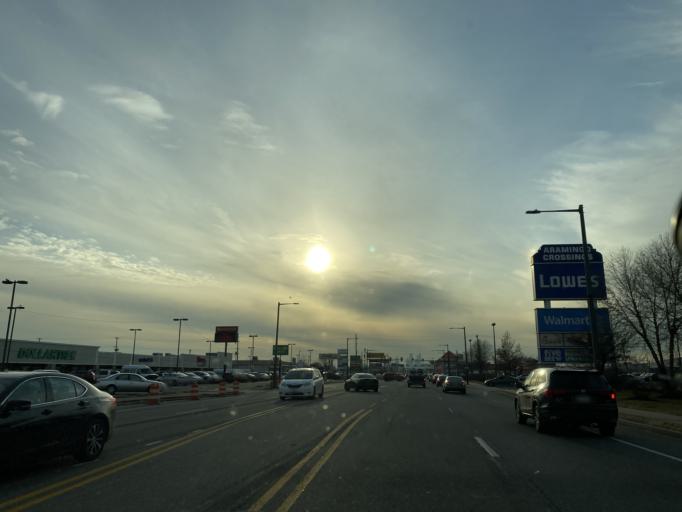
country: US
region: New Jersey
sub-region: Camden County
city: Pennsauken
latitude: 39.9970
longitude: -75.0903
